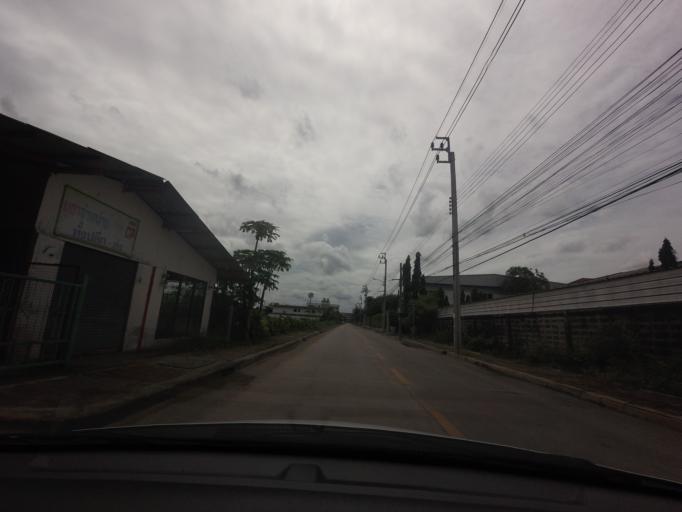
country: TH
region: Bangkok
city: Min Buri
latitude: 13.7919
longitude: 100.7506
